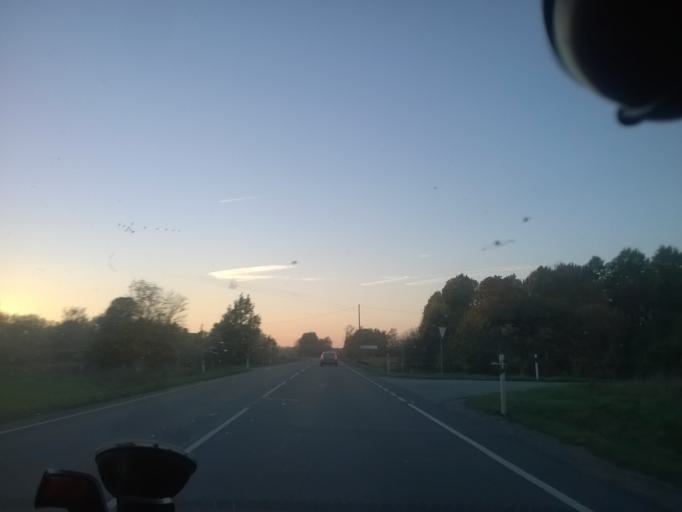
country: EE
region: Laeaene
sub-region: Ridala Parish
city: Uuemoisa
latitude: 58.9725
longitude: 23.8623
